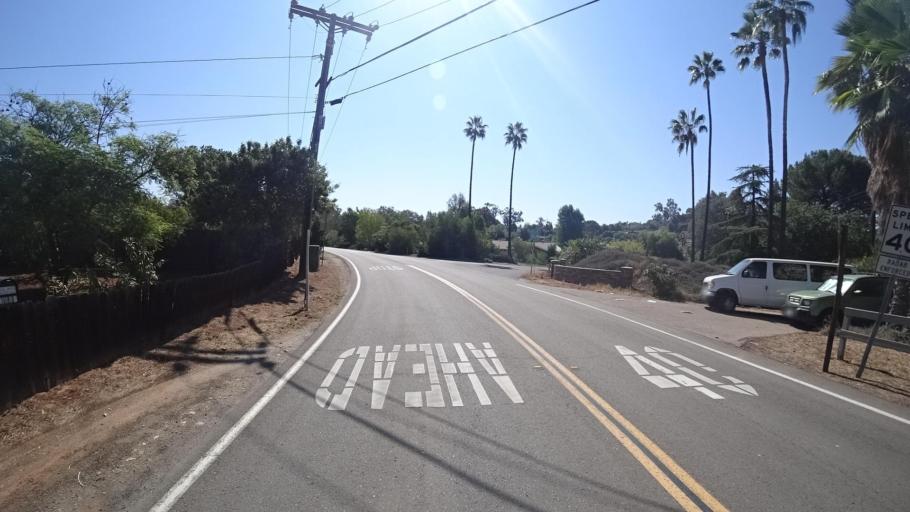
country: US
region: California
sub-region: San Diego County
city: Granite Hills
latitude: 32.7957
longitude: -116.9144
